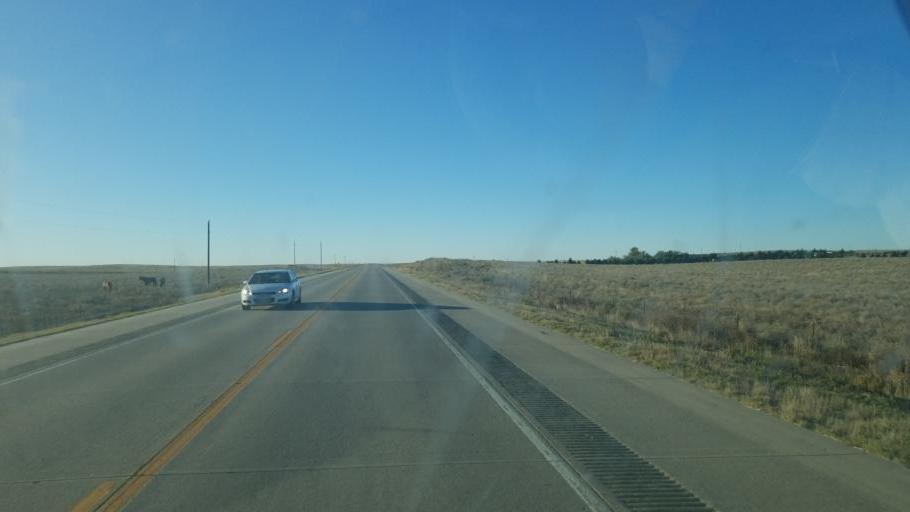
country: US
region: Colorado
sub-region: Kiowa County
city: Eads
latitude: 38.5896
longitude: -102.7861
